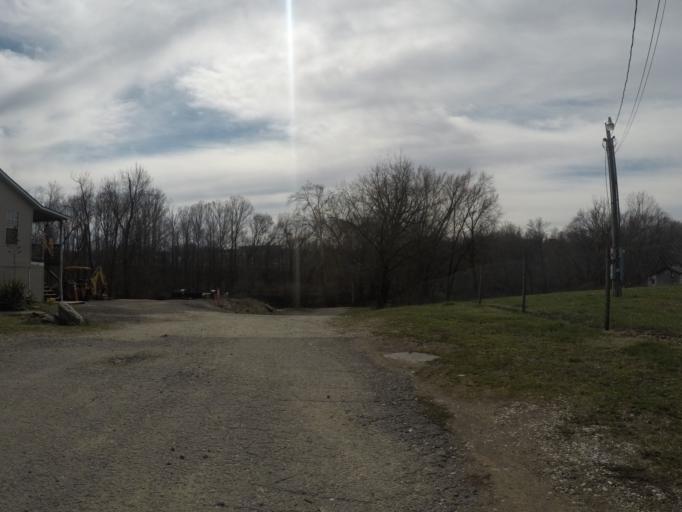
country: US
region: West Virginia
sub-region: Cabell County
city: Pea Ridge
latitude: 38.4167
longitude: -82.3502
